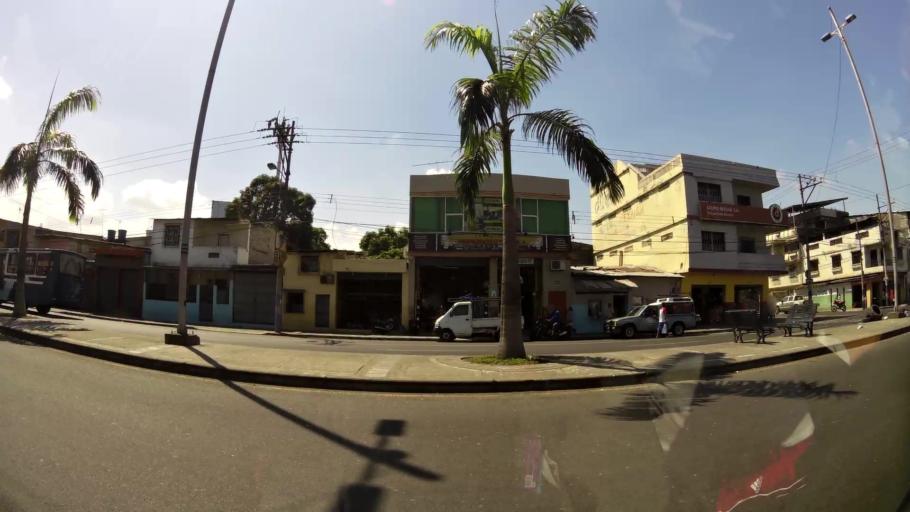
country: EC
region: Guayas
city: Guayaquil
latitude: -2.1979
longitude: -79.9317
